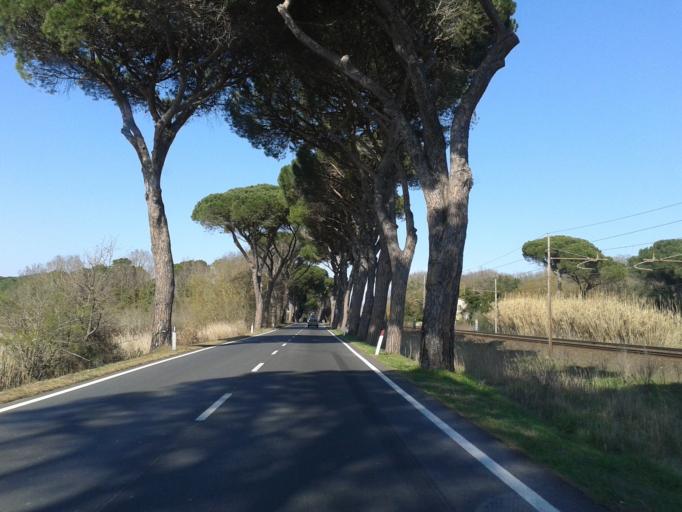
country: IT
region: Tuscany
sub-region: Province of Pisa
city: Pisa
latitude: 43.6514
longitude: 10.3635
